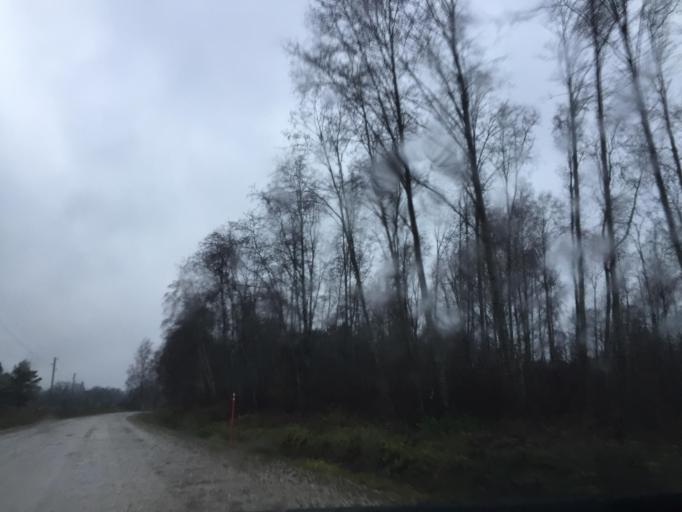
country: LV
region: Salacgrivas
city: Salacgriva
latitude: 57.7659
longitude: 24.4699
